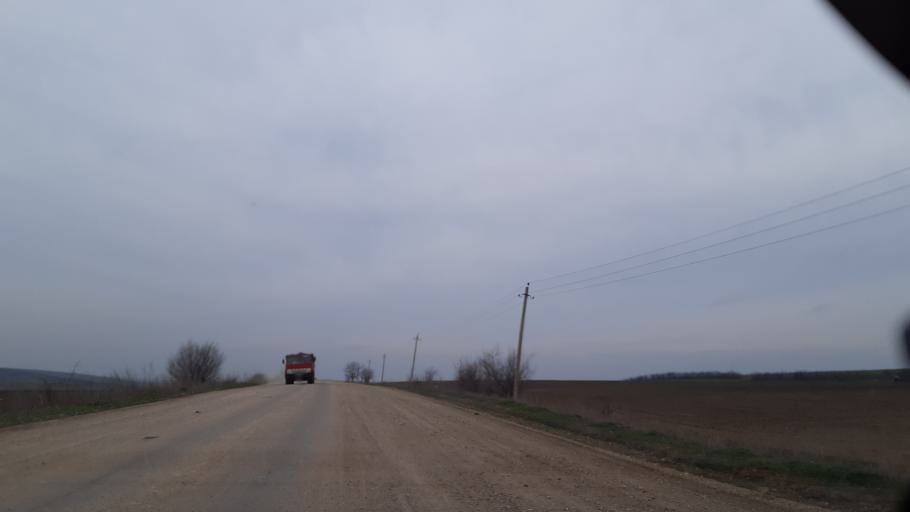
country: MD
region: Soldanesti
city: Soldanesti
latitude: 47.5907
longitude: 28.6477
